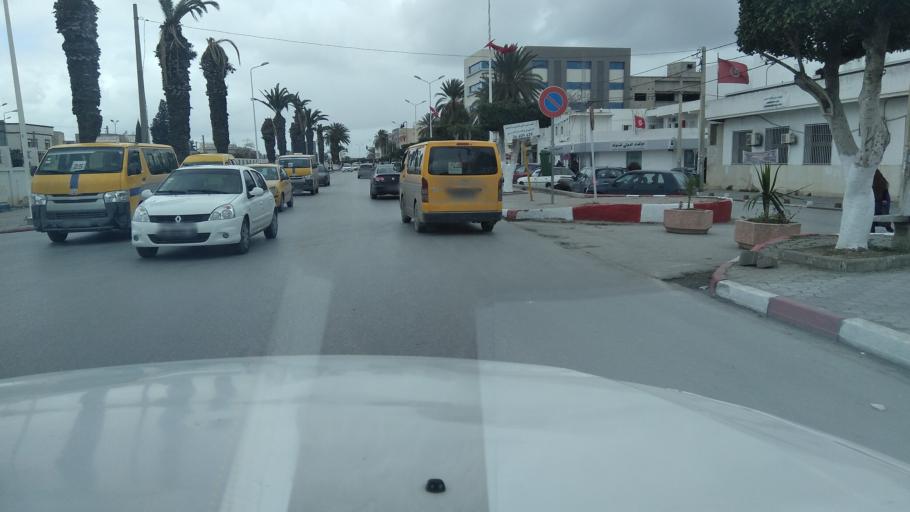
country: TN
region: Bin 'Arus
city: Ben Arous
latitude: 36.7547
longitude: 10.2216
